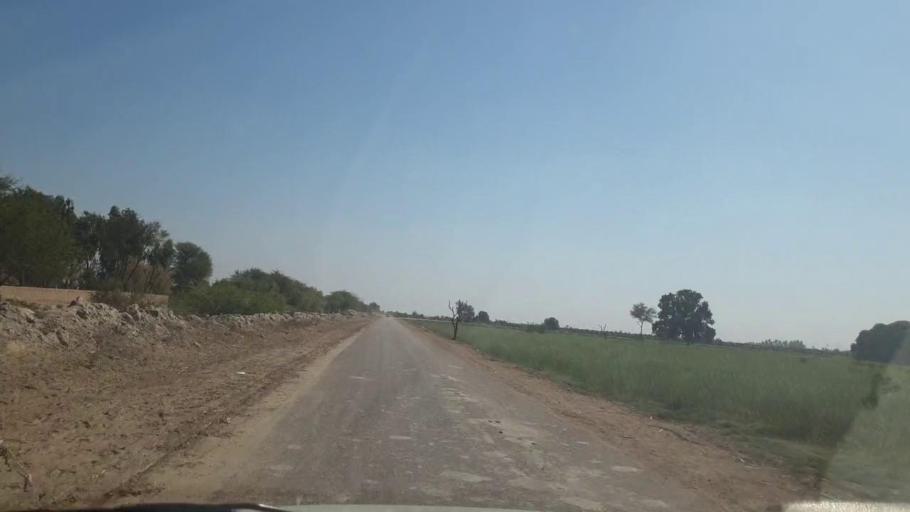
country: PK
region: Sindh
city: Mirpur Khas
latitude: 25.4624
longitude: 69.1803
